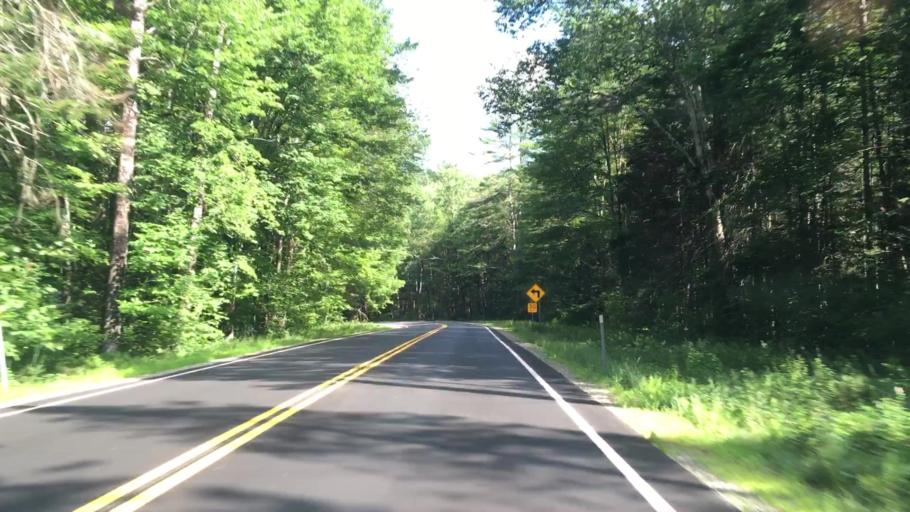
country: US
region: New Hampshire
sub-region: Grafton County
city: North Haverhill
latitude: 44.1009
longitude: -71.8616
